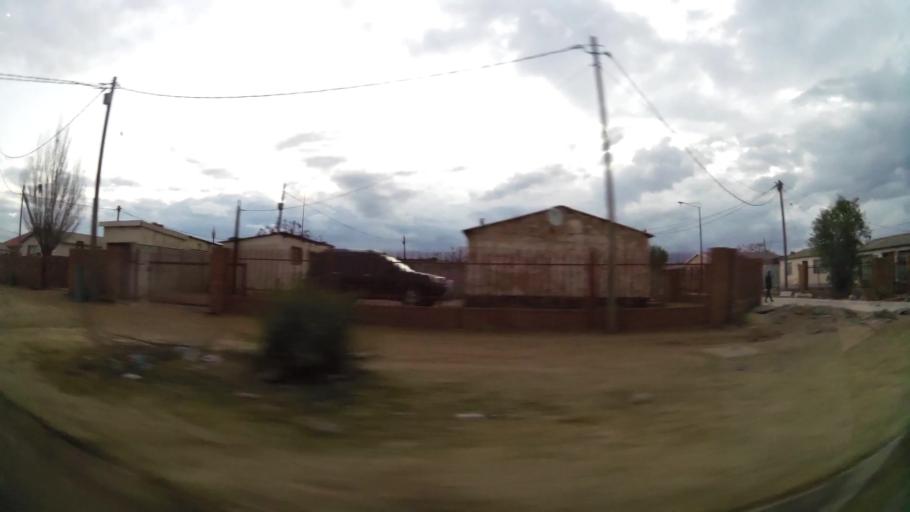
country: ZA
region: Orange Free State
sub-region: Lejweleputswa District Municipality
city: Welkom
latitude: -27.9576
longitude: 26.7855
